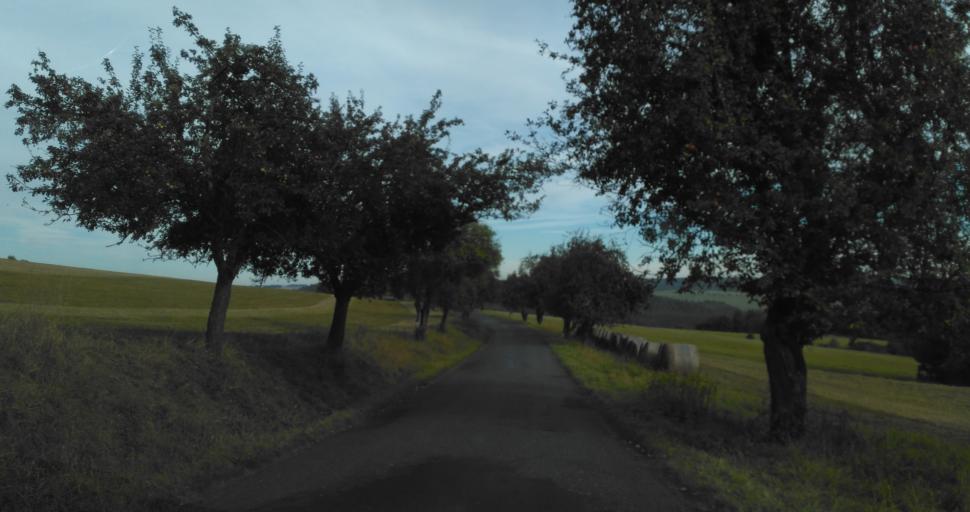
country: CZ
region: Plzensky
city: Zbiroh
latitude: 49.9552
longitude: 13.7749
